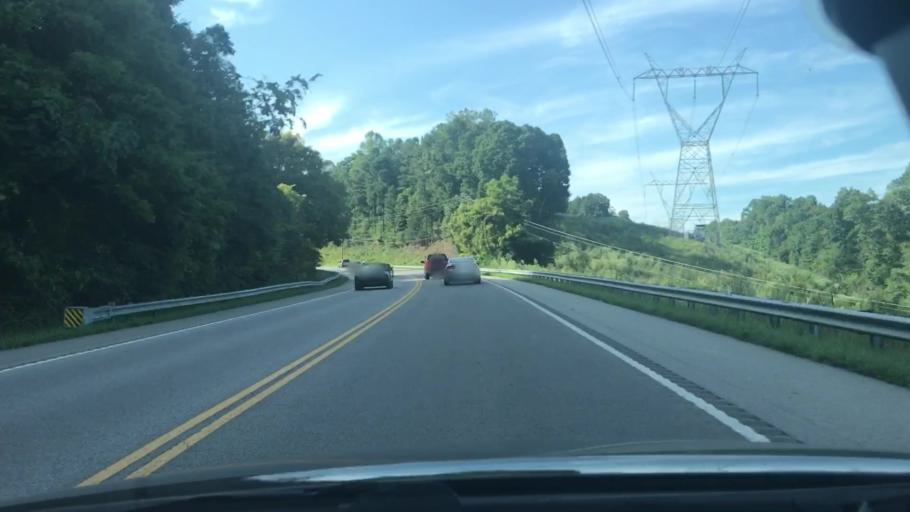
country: US
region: Tennessee
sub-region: Williamson County
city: Franklin
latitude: 35.9656
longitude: -86.9686
